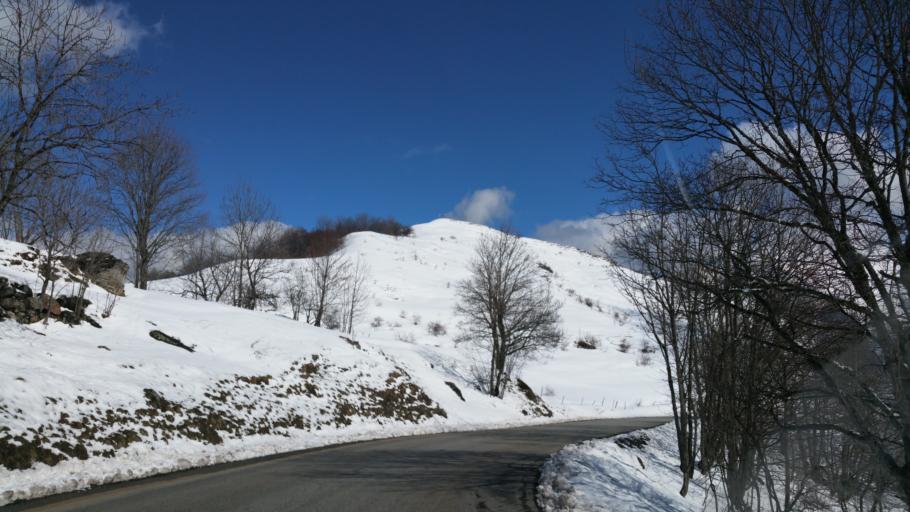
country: FR
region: Rhone-Alpes
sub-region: Departement de la Savoie
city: Saint-Jean-de-Maurienne
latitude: 45.2598
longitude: 6.2910
